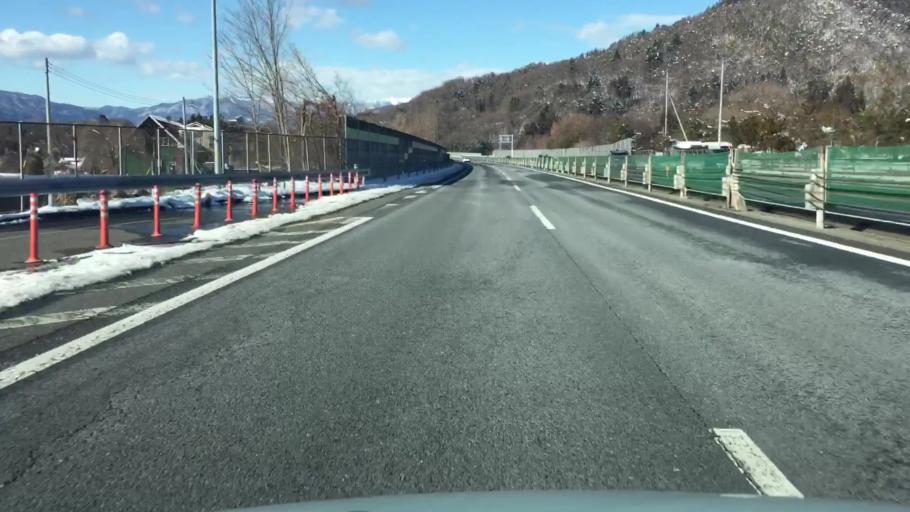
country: JP
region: Gunma
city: Numata
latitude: 36.6711
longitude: 139.0453
